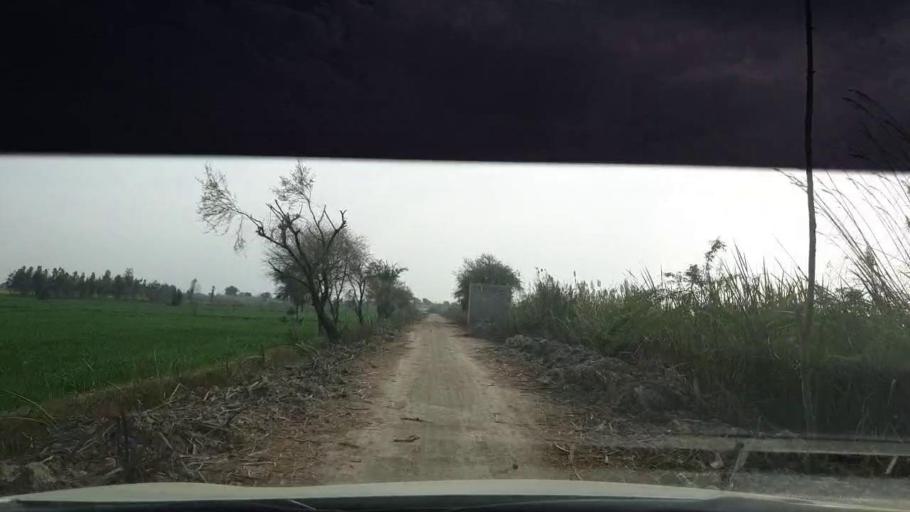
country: PK
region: Sindh
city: Berani
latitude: 25.7505
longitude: 68.8770
